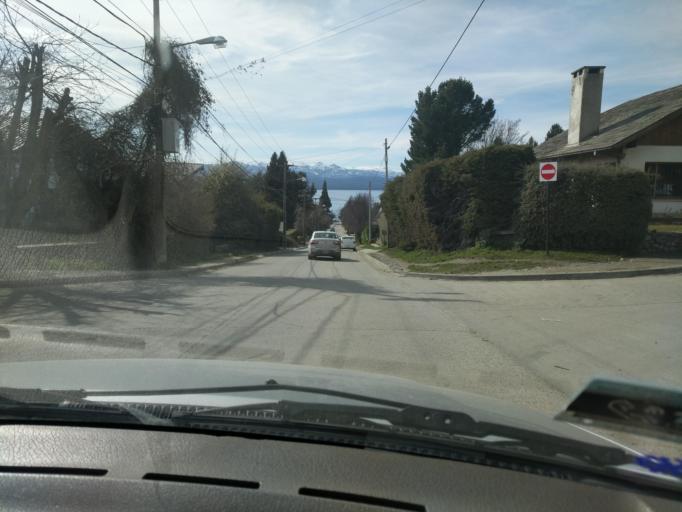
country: AR
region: Rio Negro
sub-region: Departamento de Bariloche
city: San Carlos de Bariloche
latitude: -41.1310
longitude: -71.3564
